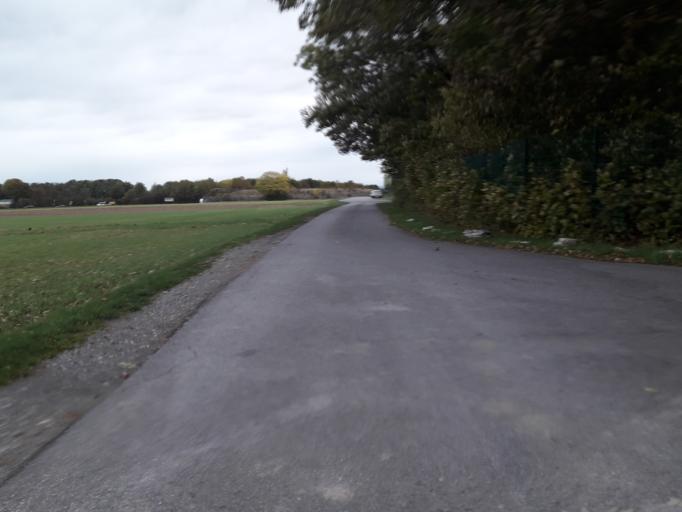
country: DE
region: North Rhine-Westphalia
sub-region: Regierungsbezirk Detmold
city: Paderborn
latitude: 51.6798
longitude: 8.7350
